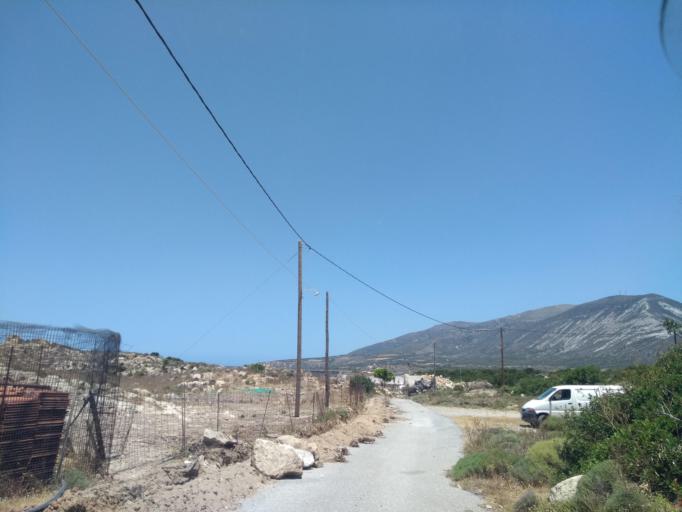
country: GR
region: Crete
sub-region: Nomos Chanias
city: Vryses
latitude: 35.3122
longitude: 23.5357
